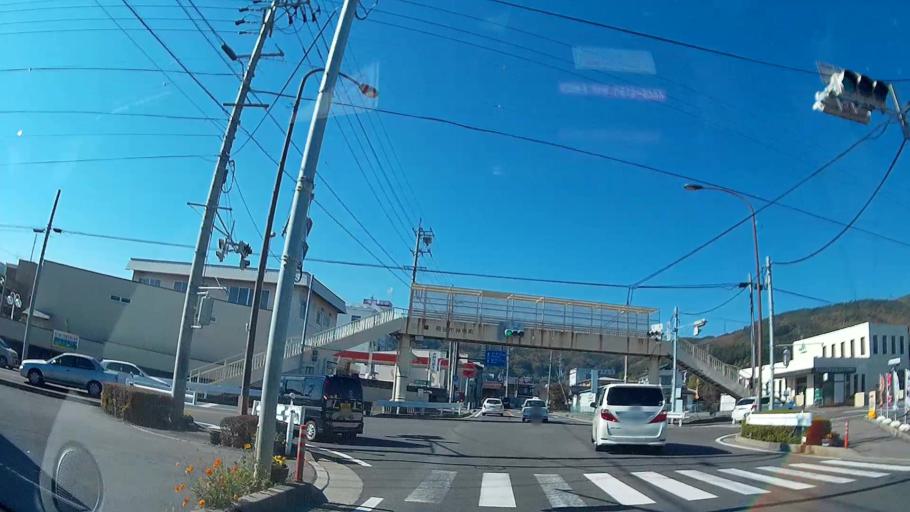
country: JP
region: Nagano
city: Okaya
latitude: 36.0822
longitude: 138.0473
